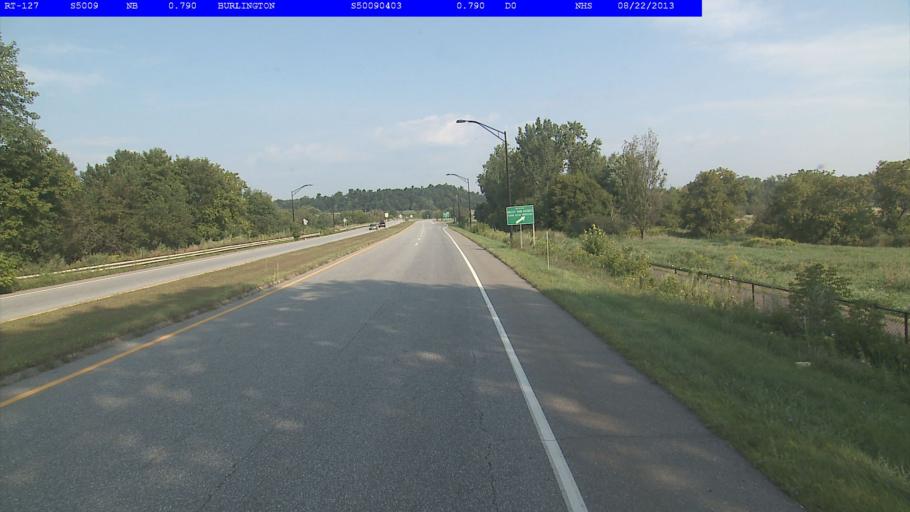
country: US
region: Vermont
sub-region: Chittenden County
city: Burlington
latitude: 44.4971
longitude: -73.2275
